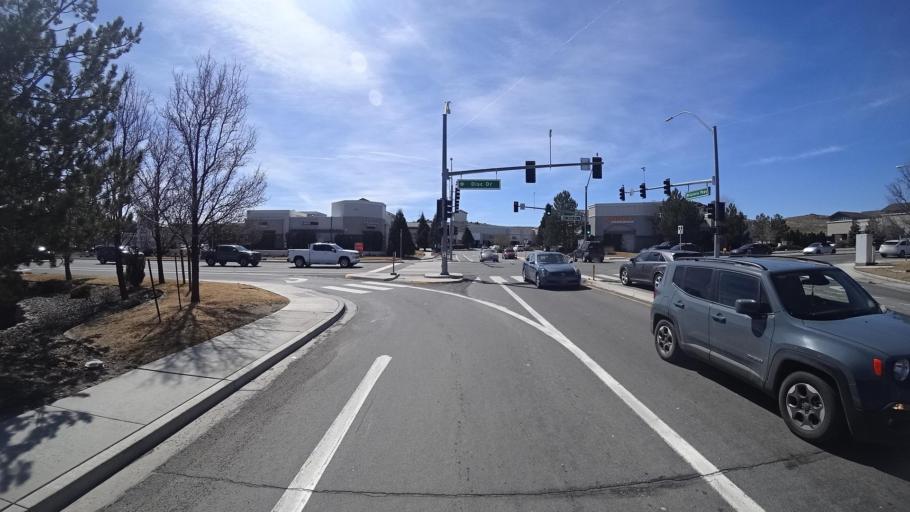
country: US
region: Nevada
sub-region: Washoe County
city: Sun Valley
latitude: 39.5766
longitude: -119.7403
